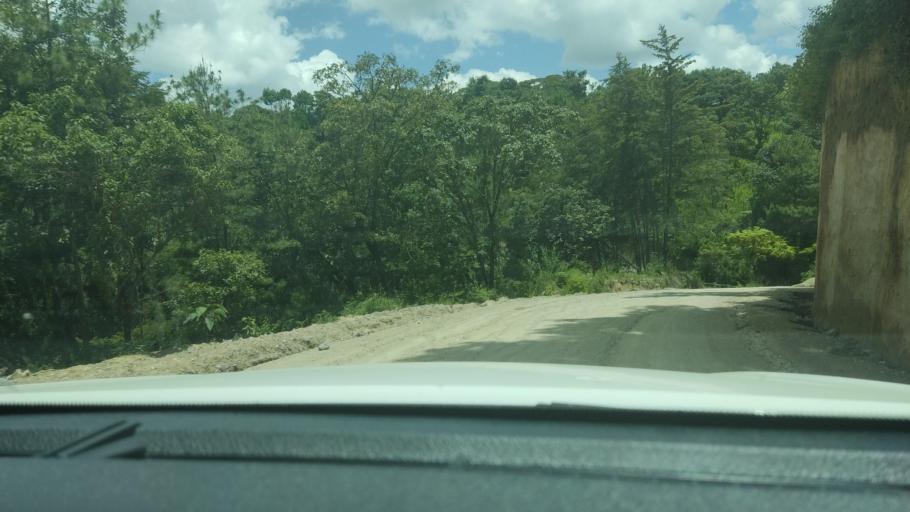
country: GT
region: Chimaltenango
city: San Martin Jilotepeque
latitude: 14.7970
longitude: -90.8124
